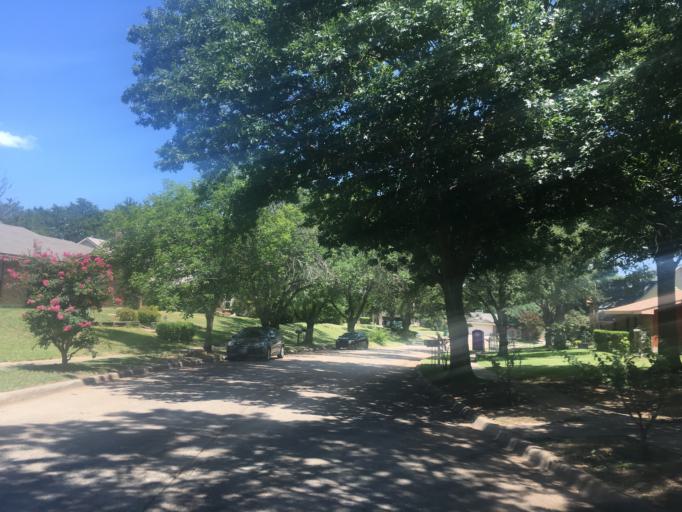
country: US
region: Texas
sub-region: Denton County
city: Lewisville
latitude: 33.0252
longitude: -97.0035
